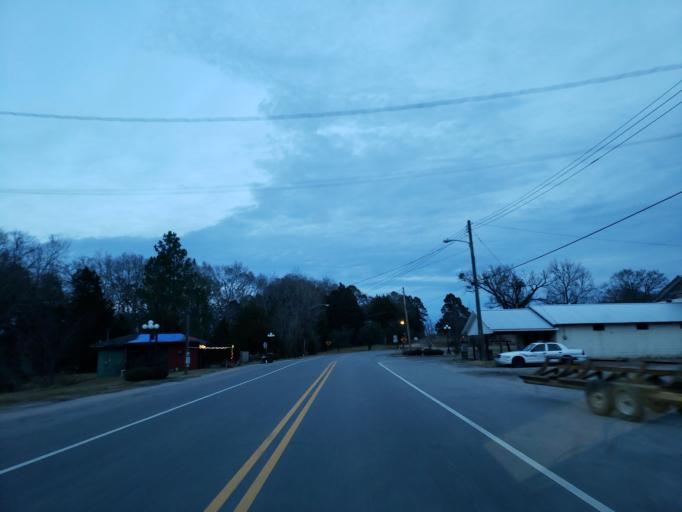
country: US
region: Alabama
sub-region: Sumter County
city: Livingston
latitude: 32.8219
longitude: -88.1599
